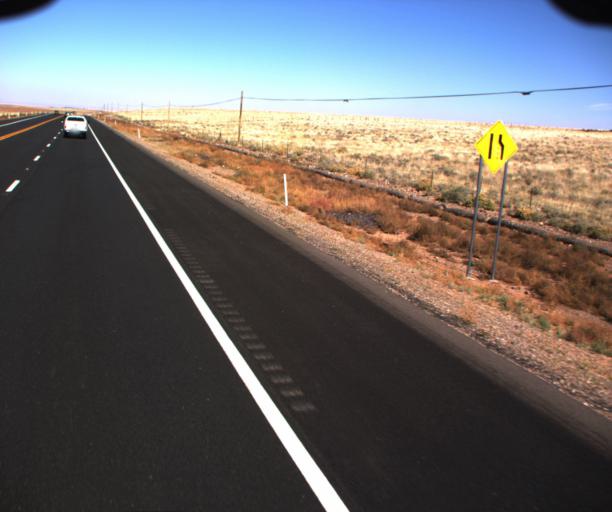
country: US
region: Arizona
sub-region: Coconino County
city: Tuba City
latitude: 35.6978
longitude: -111.5002
